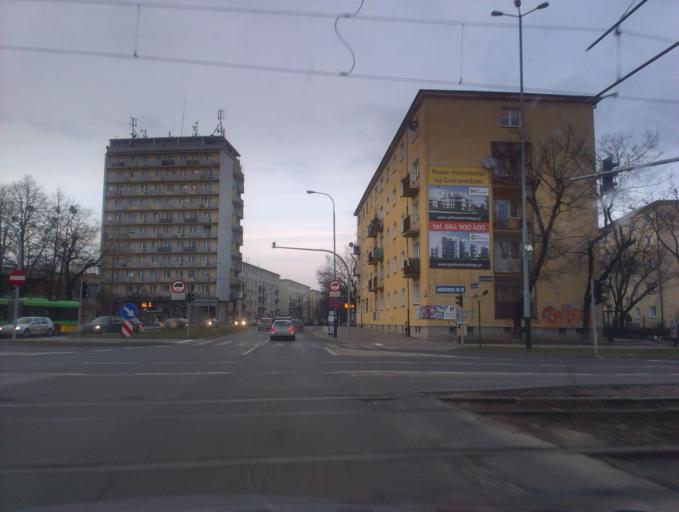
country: PL
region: Greater Poland Voivodeship
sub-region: Poznan
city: Poznan
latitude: 52.3990
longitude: 16.8767
